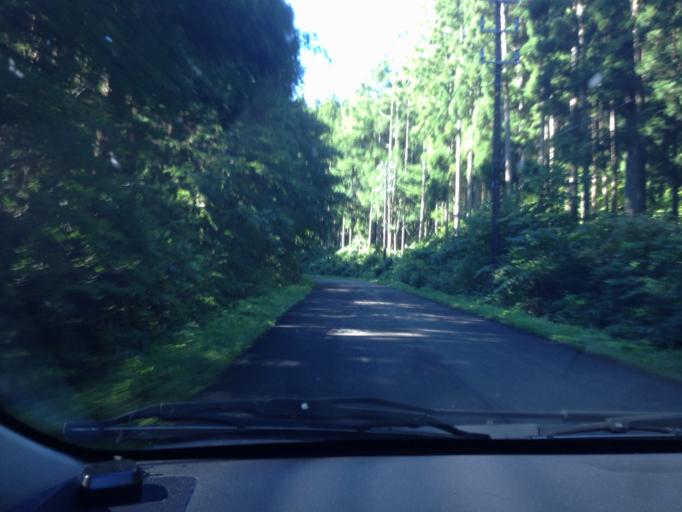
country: JP
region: Fukushima
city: Inawashiro
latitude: 37.3616
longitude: 140.0571
